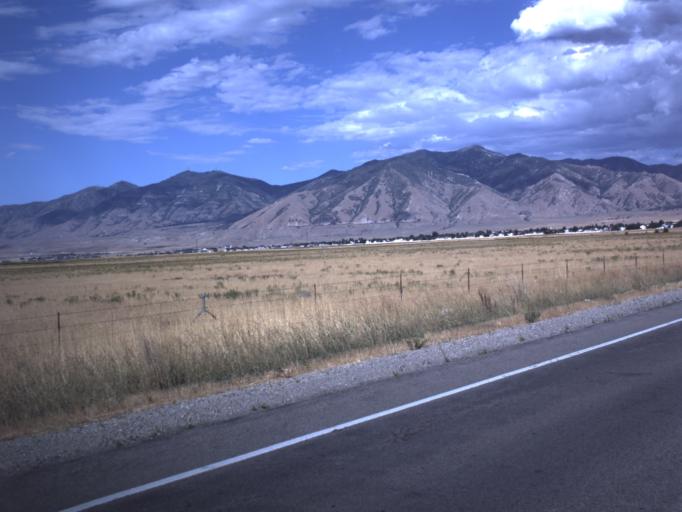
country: US
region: Utah
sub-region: Tooele County
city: Tooele
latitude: 40.5507
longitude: -112.3339
